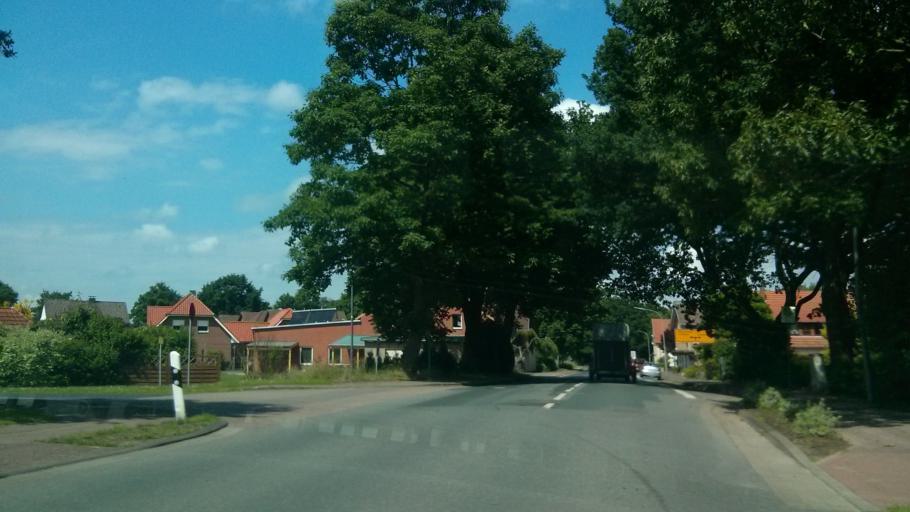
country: DE
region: Lower Saxony
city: Elmlohe
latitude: 53.5157
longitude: 8.7236
